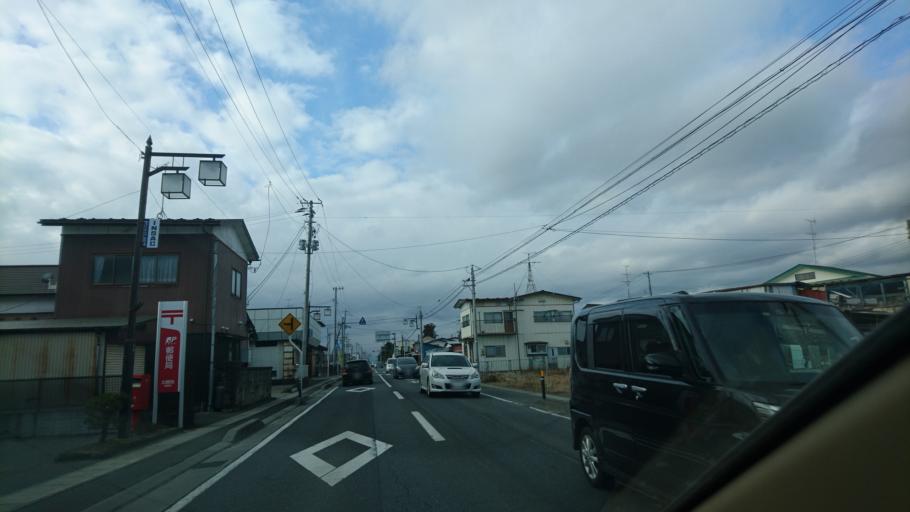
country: JP
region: Miyagi
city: Kogota
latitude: 38.5606
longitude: 141.0235
